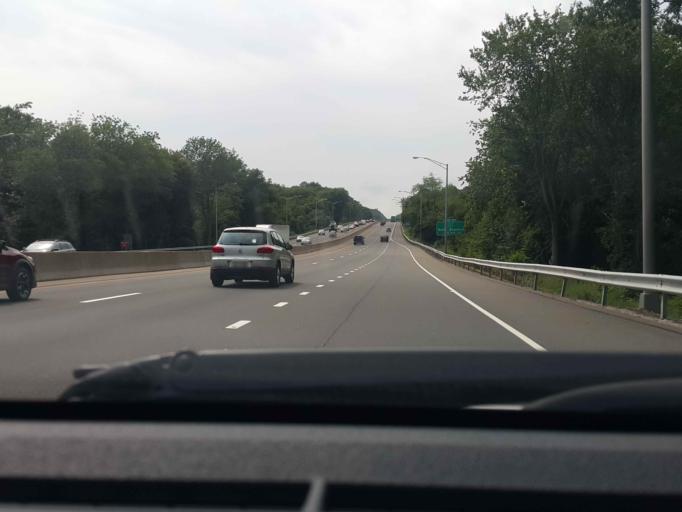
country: US
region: Connecticut
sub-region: New Haven County
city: Guilford
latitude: 41.2958
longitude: -72.6900
